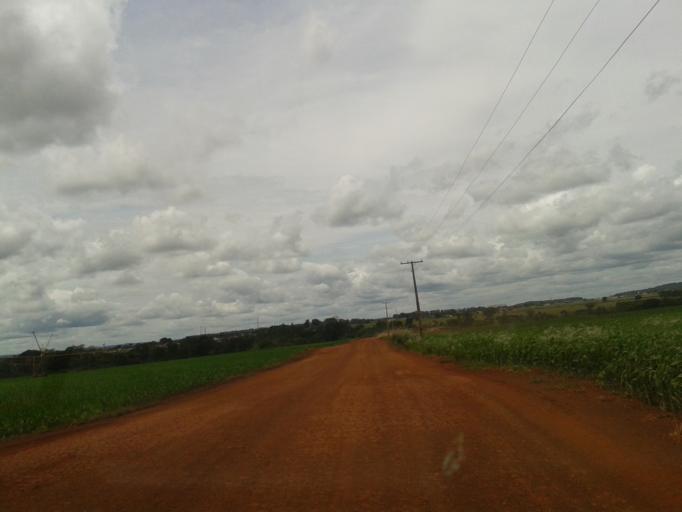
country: BR
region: Minas Gerais
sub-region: Centralina
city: Centralina
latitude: -18.5928
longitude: -49.2196
